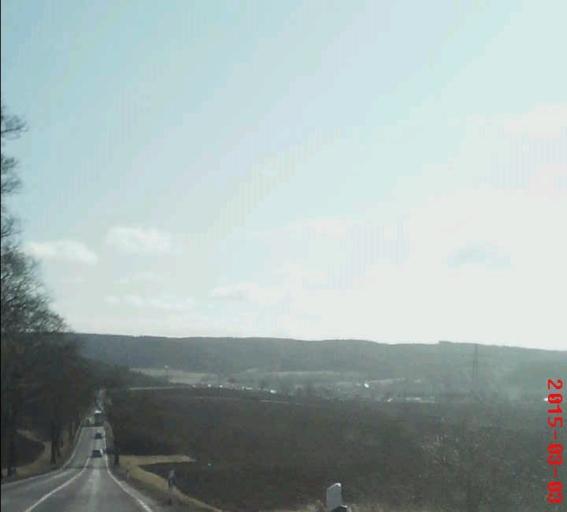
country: DE
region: Thuringia
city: Stadtilm
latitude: 50.7908
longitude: 11.0523
